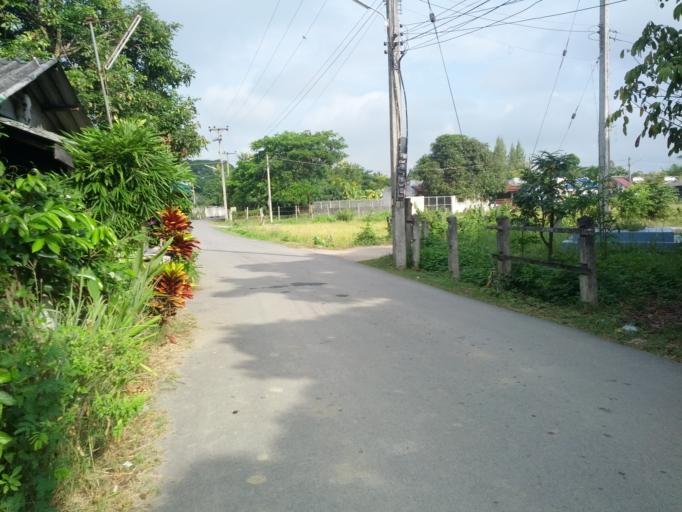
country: TH
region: Chiang Mai
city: San Kamphaeng
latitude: 18.7875
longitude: 99.1028
